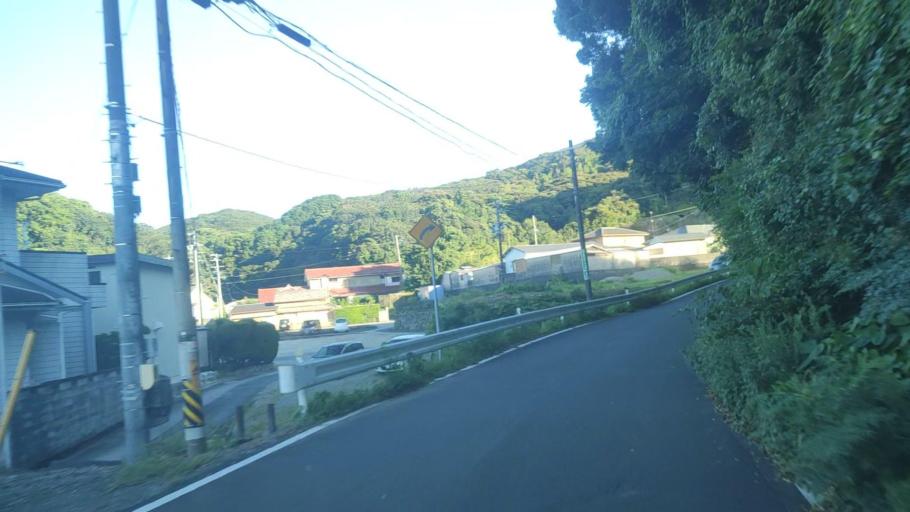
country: JP
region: Mie
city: Ise
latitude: 34.2753
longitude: 136.7693
